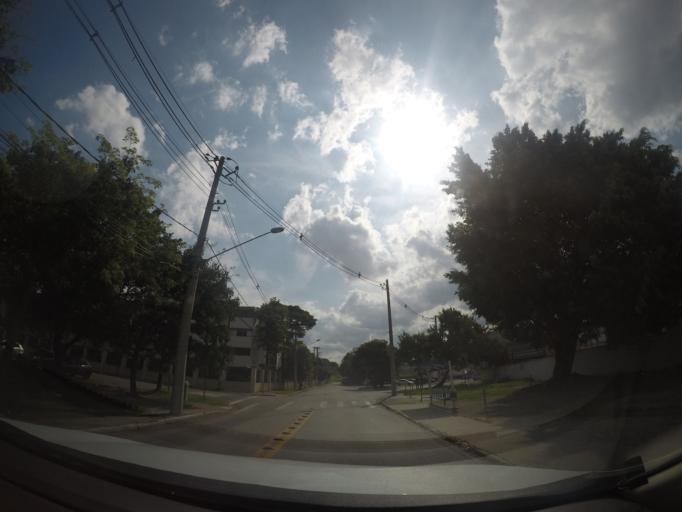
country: BR
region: Sao Paulo
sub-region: Guarulhos
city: Guarulhos
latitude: -23.4497
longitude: -46.4989
